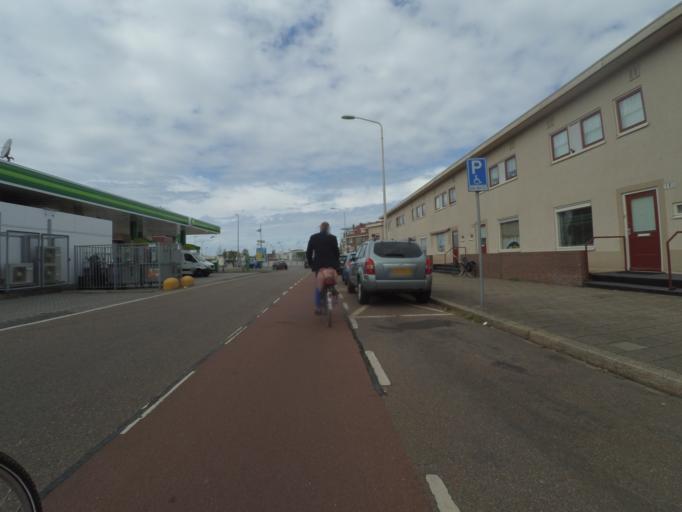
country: NL
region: South Holland
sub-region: Gemeente Den Haag
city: Scheveningen
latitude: 52.0965
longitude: 4.2712
